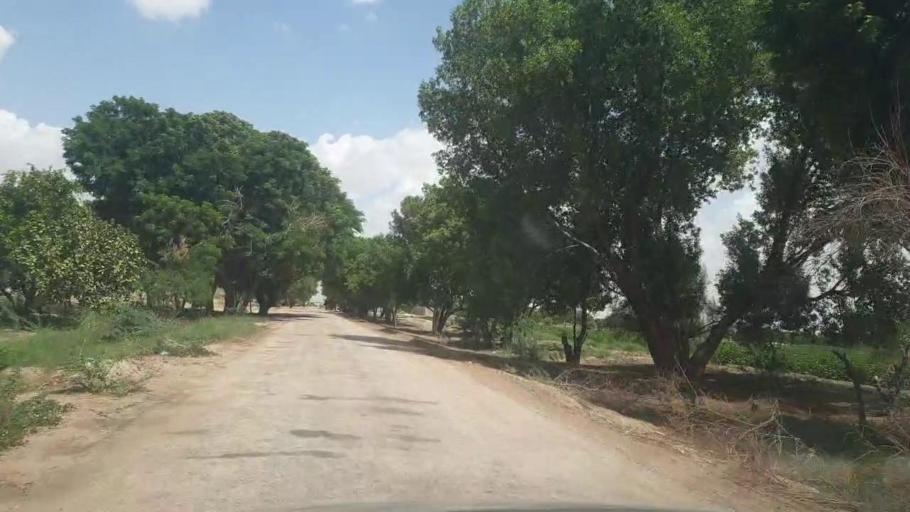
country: PK
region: Sindh
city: Kot Diji
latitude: 27.2191
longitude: 69.0525
